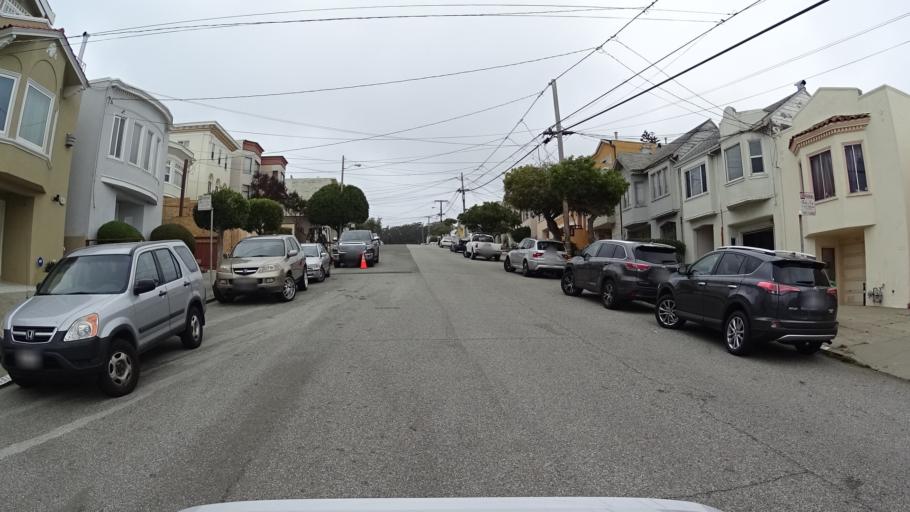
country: US
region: California
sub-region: San Francisco County
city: San Francisco
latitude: 37.7777
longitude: -122.4996
